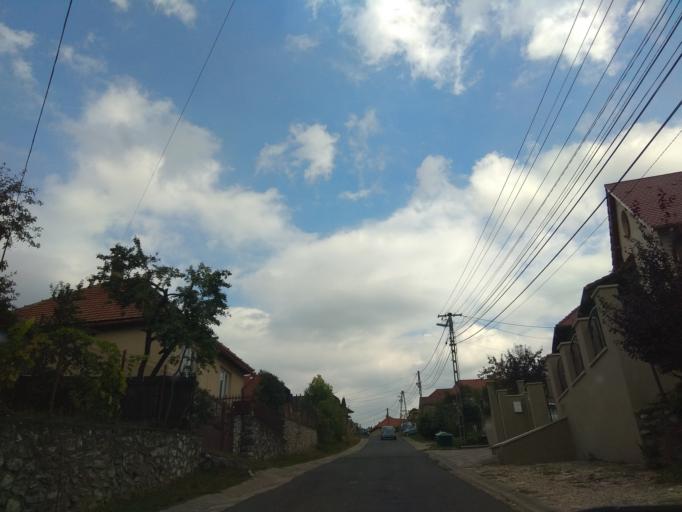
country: HU
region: Borsod-Abauj-Zemplen
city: Saly
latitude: 48.0690
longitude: 20.6381
